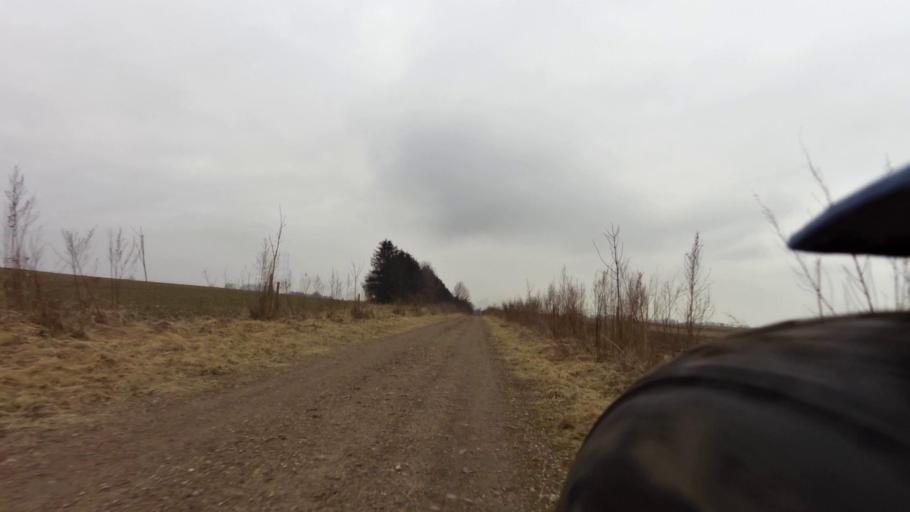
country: PL
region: West Pomeranian Voivodeship
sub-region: Powiat walecki
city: Walcz
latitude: 53.2389
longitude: 16.4645
